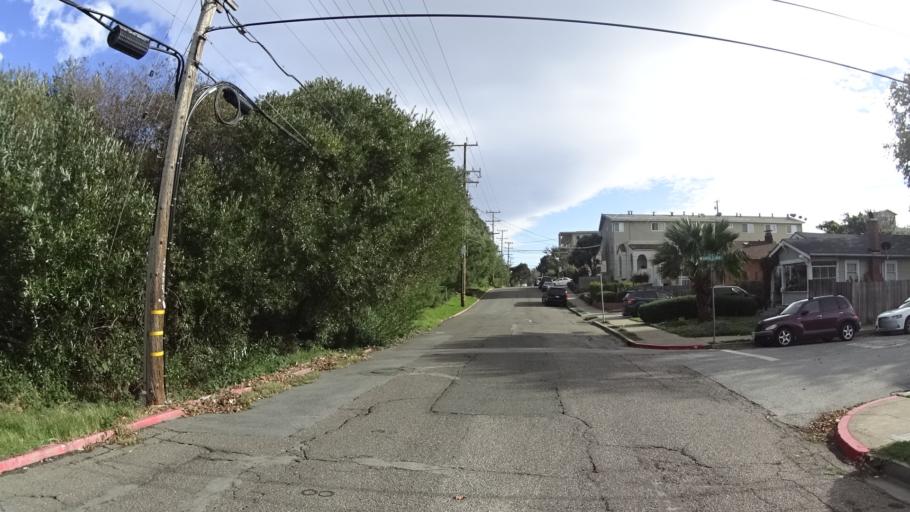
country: US
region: California
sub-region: San Mateo County
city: San Bruno
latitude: 37.6147
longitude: -122.4017
